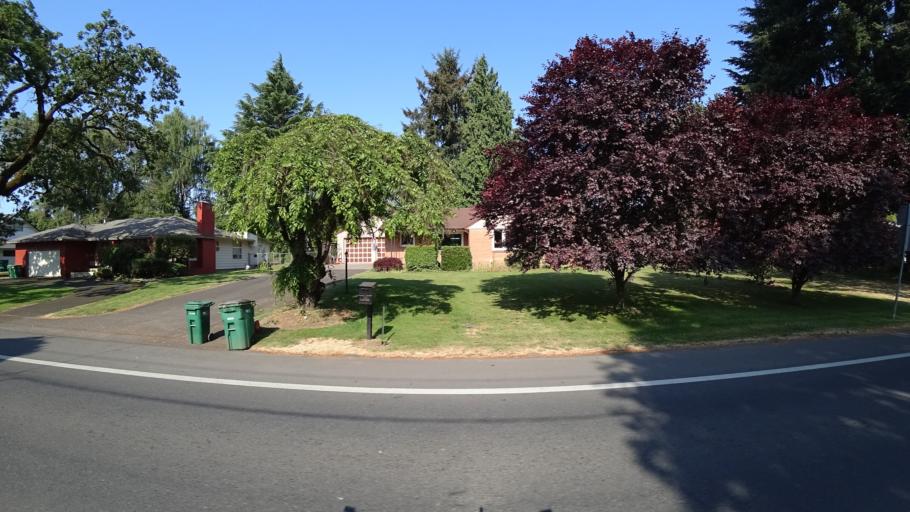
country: US
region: Oregon
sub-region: Clackamas County
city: Oatfield
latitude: 45.4437
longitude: -122.5992
